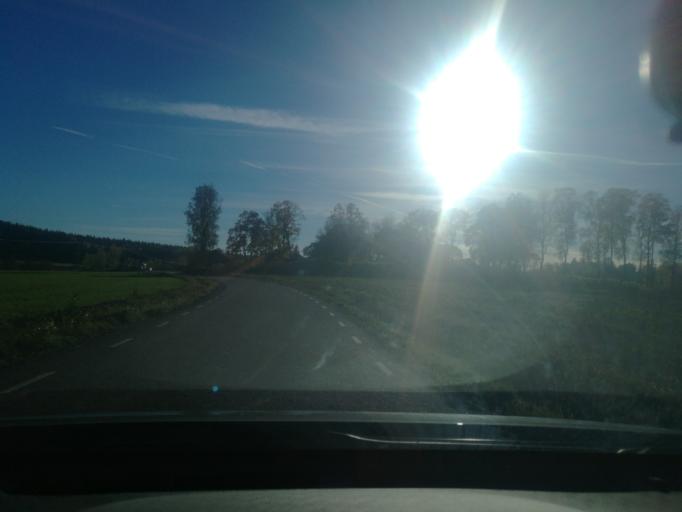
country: SE
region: Vaestmanland
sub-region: Kopings Kommun
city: Koping
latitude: 59.5971
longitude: 16.0024
